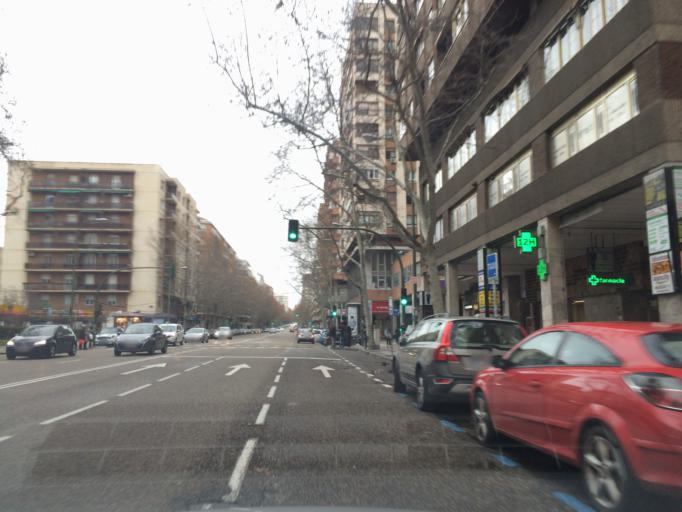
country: ES
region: Madrid
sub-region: Provincia de Madrid
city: Chamberi
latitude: 40.4489
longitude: -3.6953
